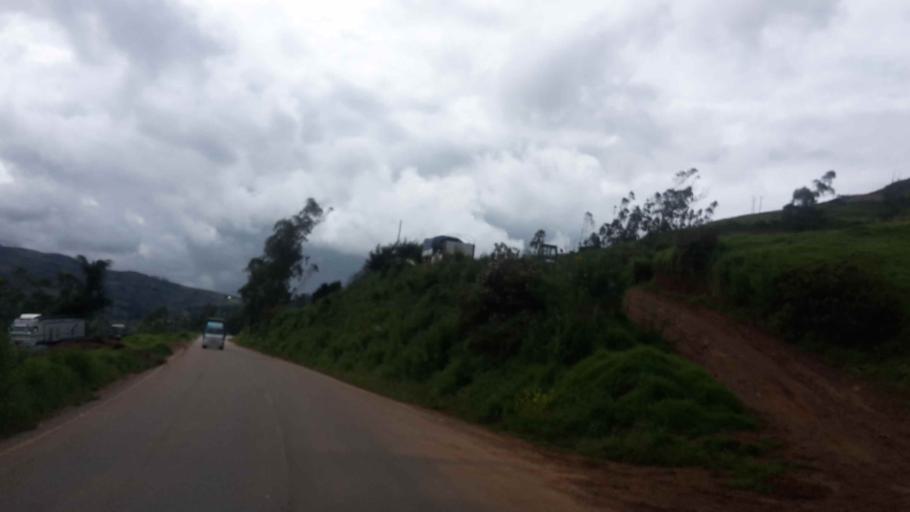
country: BO
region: Cochabamba
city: Totora
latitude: -17.5466
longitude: -65.3578
